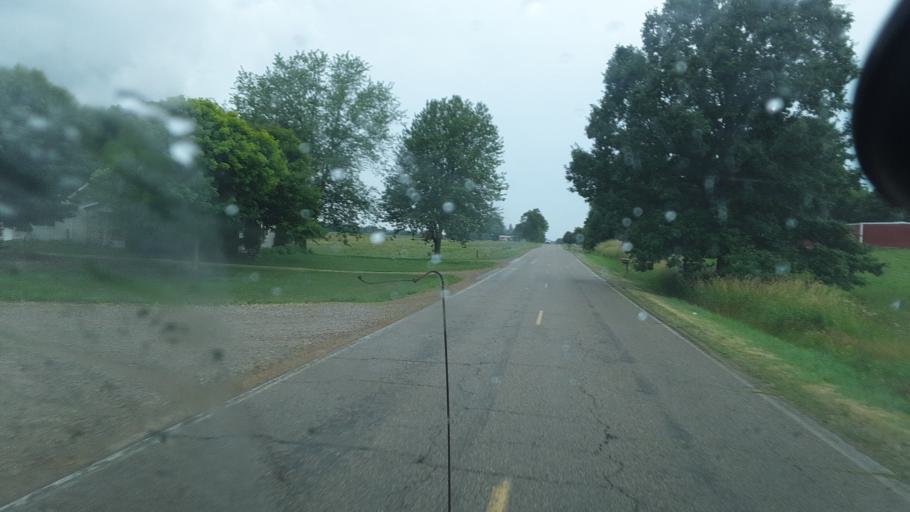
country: US
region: Michigan
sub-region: Hillsdale County
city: Reading
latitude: 41.7081
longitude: -84.7305
